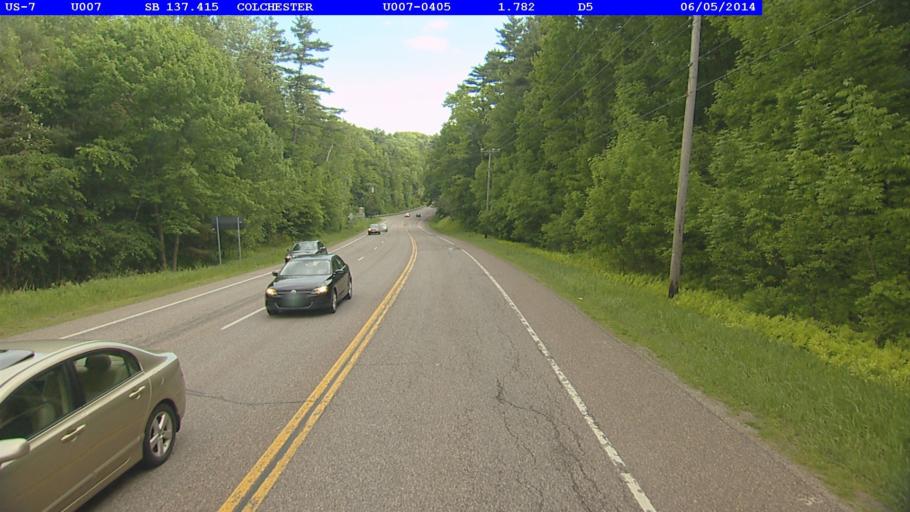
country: US
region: Vermont
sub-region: Chittenden County
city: Colchester
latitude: 44.5259
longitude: -73.1730
